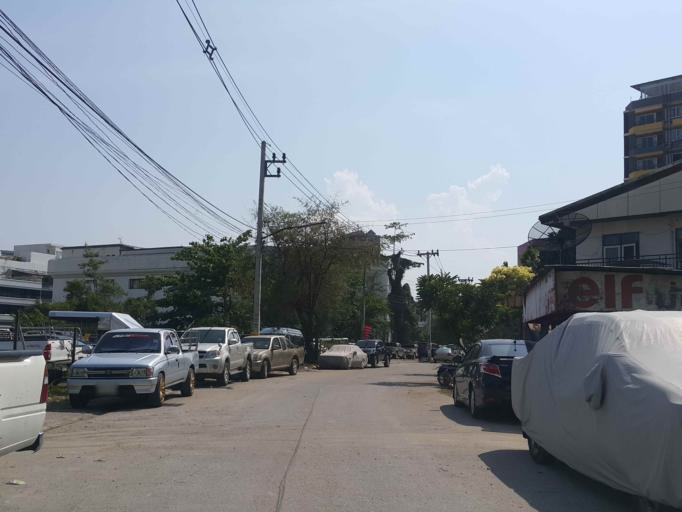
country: TH
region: Chiang Mai
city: Chiang Mai
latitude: 18.7770
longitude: 99.0007
